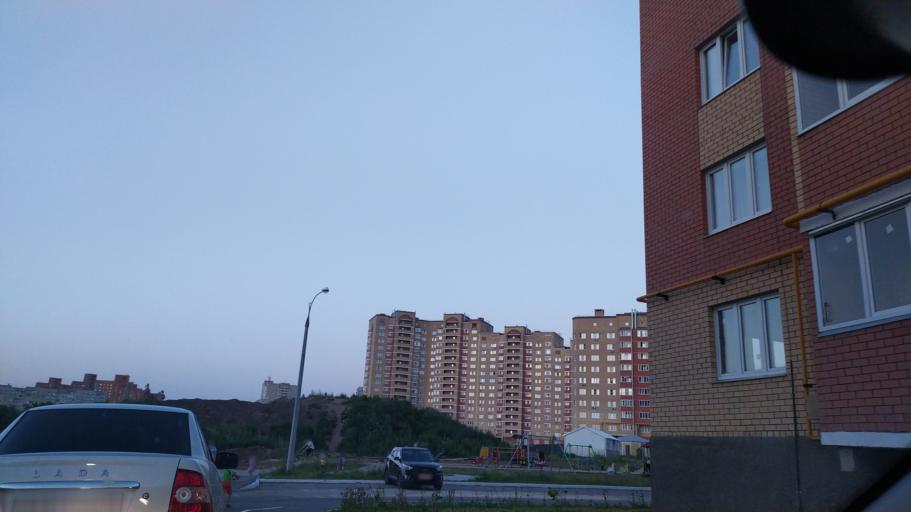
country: RU
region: Chuvashia
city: Novyye Lapsary
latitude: 56.1344
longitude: 47.1497
